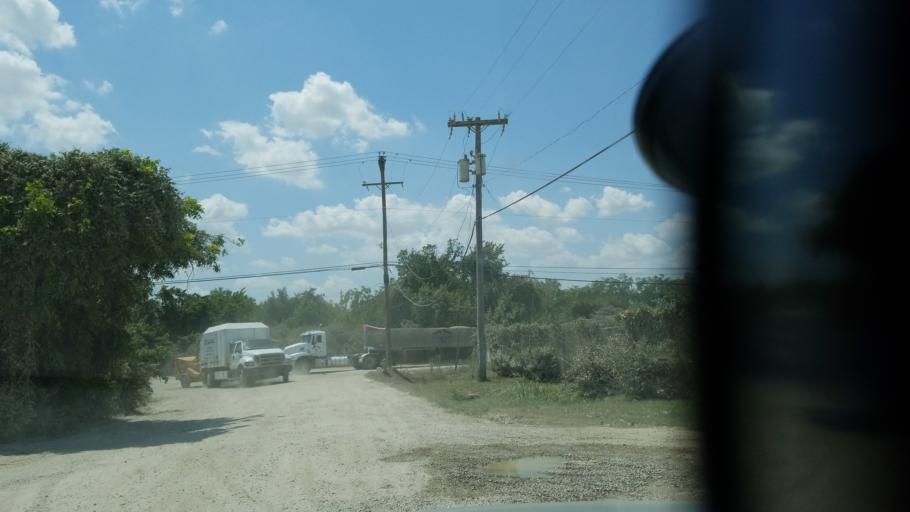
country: US
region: Texas
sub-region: Dallas County
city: Farmers Branch
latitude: 32.8761
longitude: -96.9192
